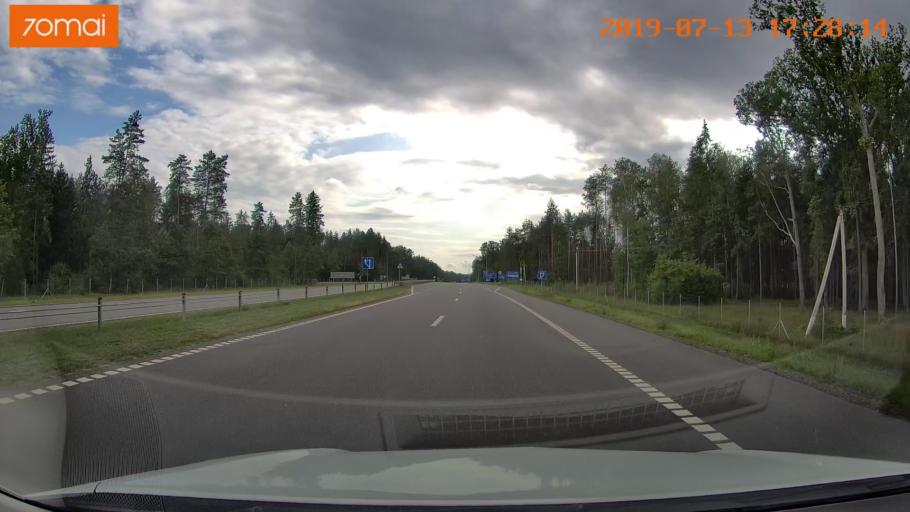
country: BY
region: Mogilev
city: Babruysk
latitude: 53.2359
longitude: 29.1411
